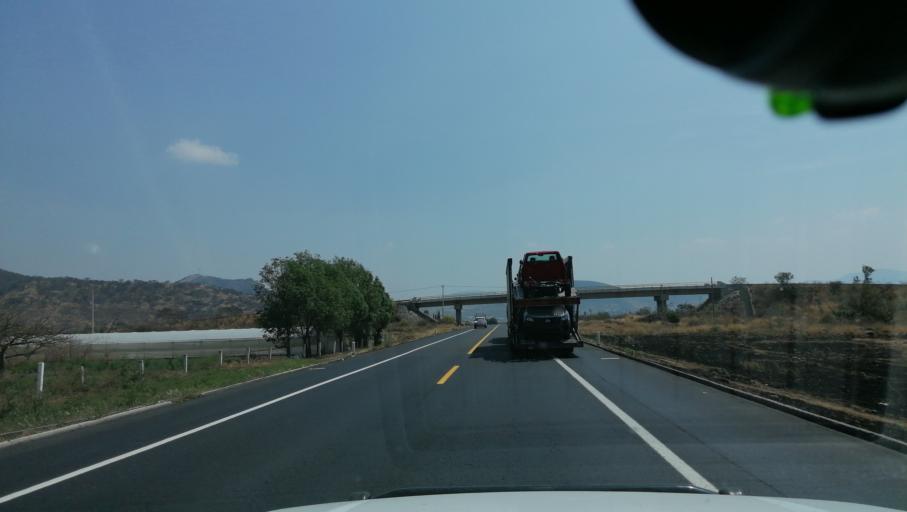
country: MX
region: Puebla
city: San Juan Tianguismanalco
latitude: 18.9341
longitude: -98.4560
